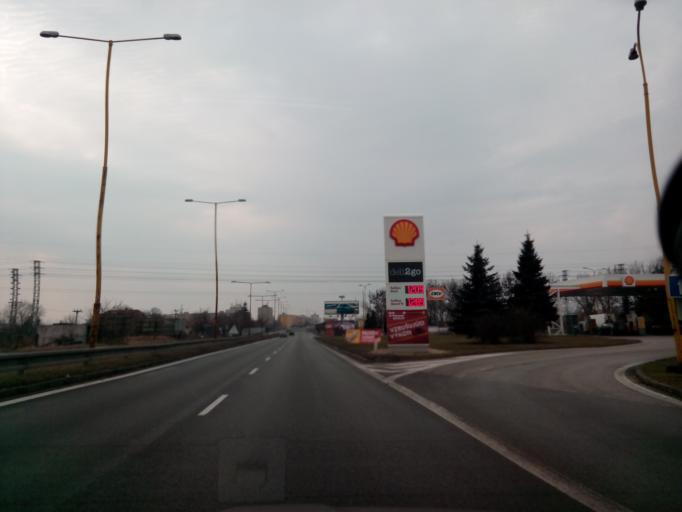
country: SK
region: Kosicky
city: Kosice
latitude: 48.7042
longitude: 21.2797
